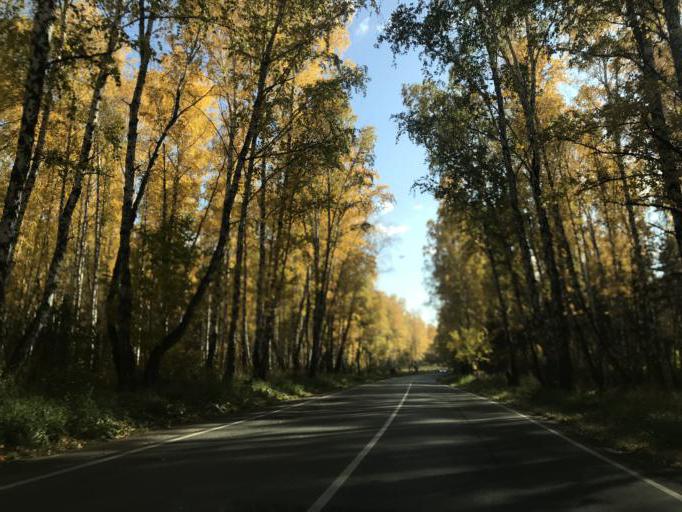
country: RU
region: Chelyabinsk
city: Dolgoderevenskoye
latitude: 55.2722
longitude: 61.3649
